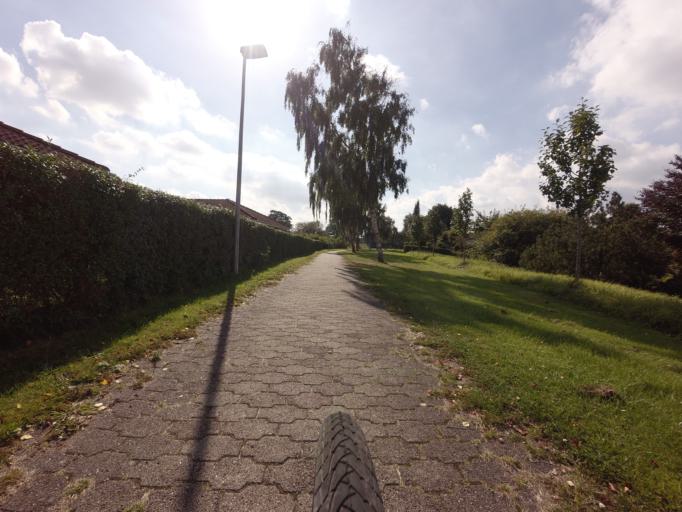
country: DK
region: Central Jutland
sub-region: Viborg Kommune
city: Viborg
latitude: 56.3626
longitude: 9.2983
